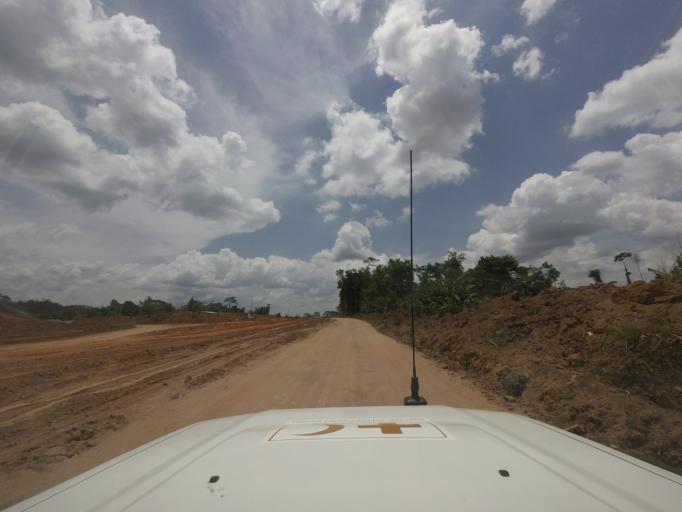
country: LR
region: Nimba
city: Sanniquellie
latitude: 7.2372
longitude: -8.8822
